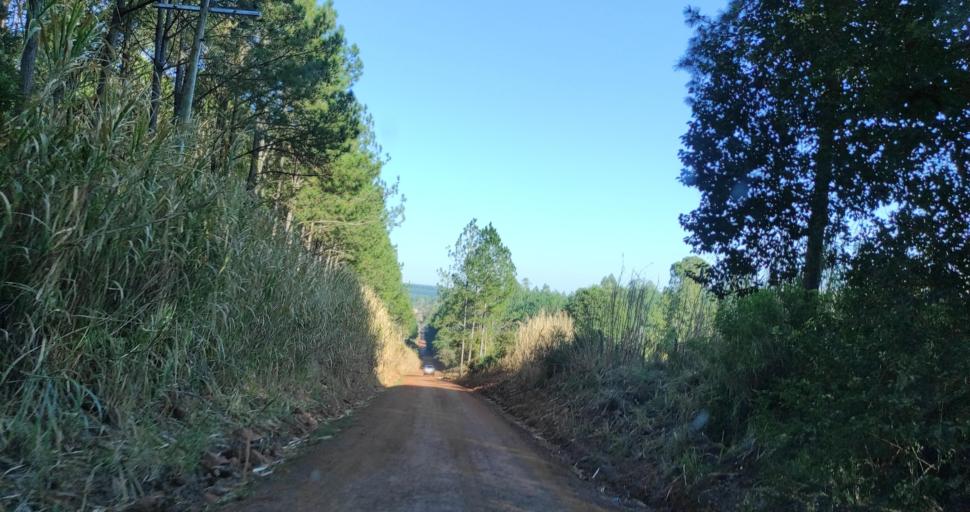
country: AR
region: Misiones
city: Puerto Rico
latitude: -26.8645
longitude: -55.0338
